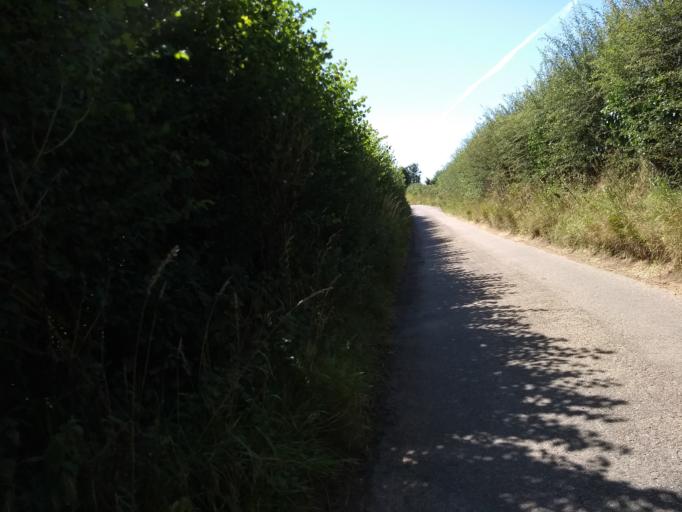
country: GB
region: England
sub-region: Isle of Wight
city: Brading
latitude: 50.6743
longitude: -1.1600
